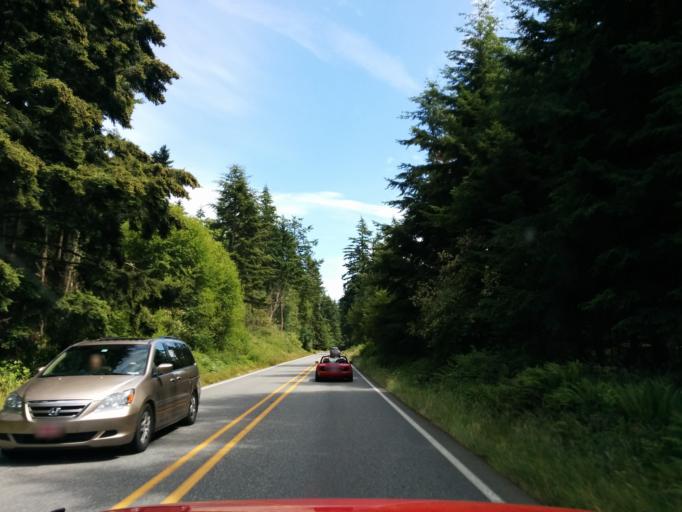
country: US
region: Washington
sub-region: Island County
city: Coupeville
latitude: 48.1822
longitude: -122.6247
